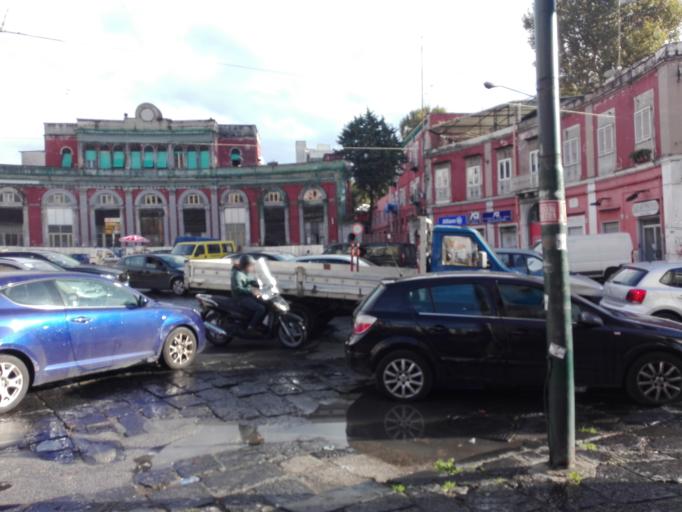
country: IT
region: Campania
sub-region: Provincia di Napoli
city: Napoli
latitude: 40.8654
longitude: 14.2690
